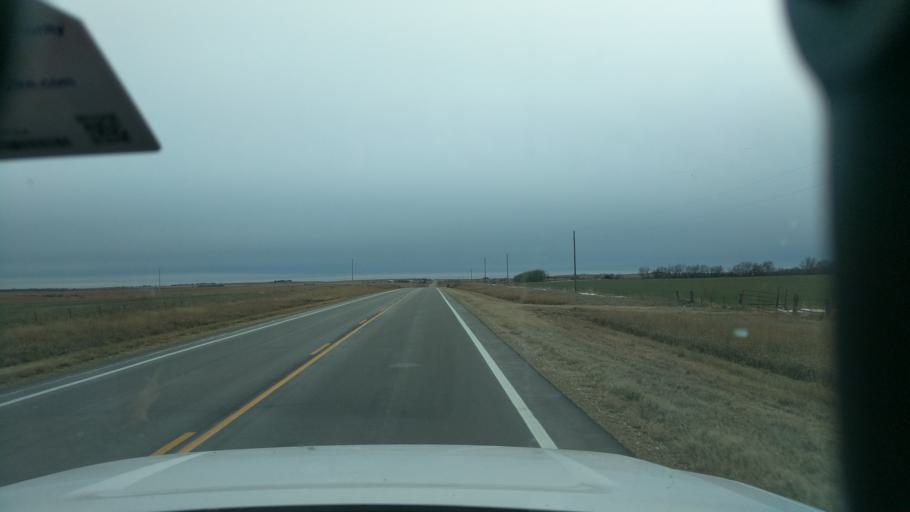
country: US
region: Kansas
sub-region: Dickinson County
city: Herington
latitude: 38.7711
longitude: -96.9273
